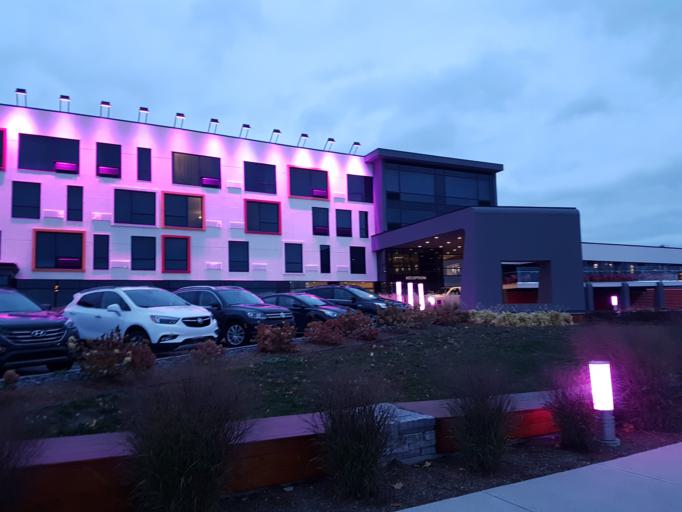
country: CA
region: Quebec
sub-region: Bas-Saint-Laurent
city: Riviere-du-Loup
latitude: 47.8290
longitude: -69.5535
